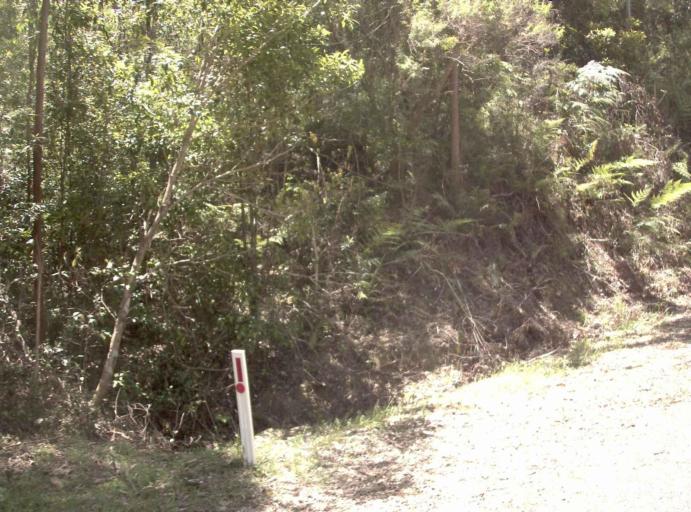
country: AU
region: New South Wales
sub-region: Bombala
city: Bombala
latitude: -37.4660
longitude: 148.9343
